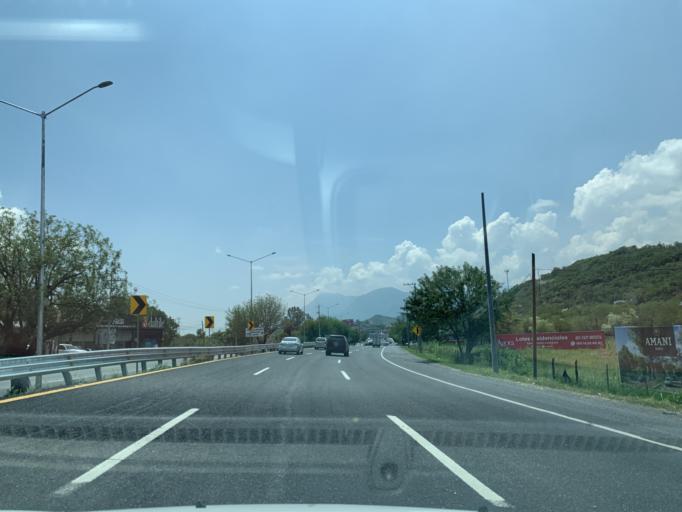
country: MX
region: Nuevo Leon
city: Santiago
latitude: 25.4391
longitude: -100.1536
